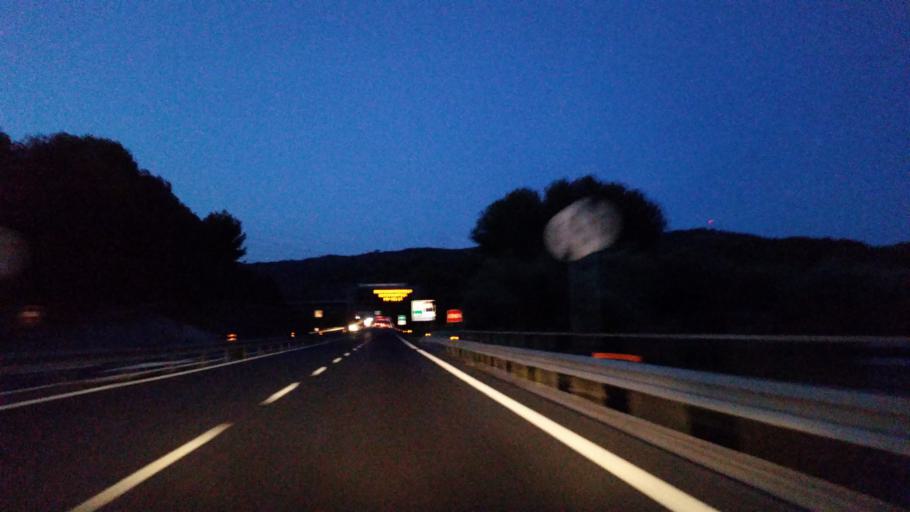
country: IT
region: Liguria
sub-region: Provincia di Imperia
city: San Bartolomeo al Mare
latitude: 43.9313
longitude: 8.1009
